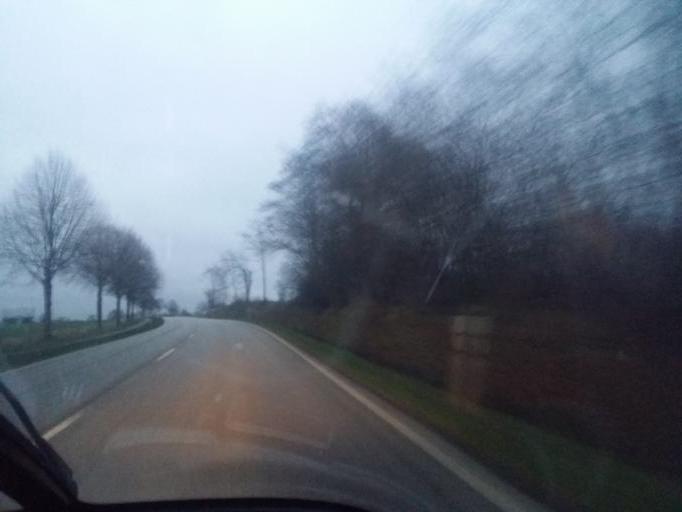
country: DE
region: Schleswig-Holstein
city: Gokels
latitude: 54.1165
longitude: 9.4561
